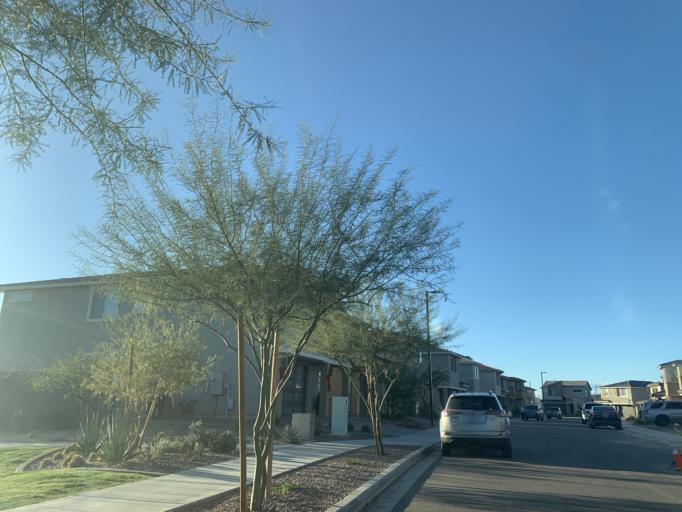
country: US
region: Arizona
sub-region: Maricopa County
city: Cave Creek
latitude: 33.6870
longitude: -112.0189
